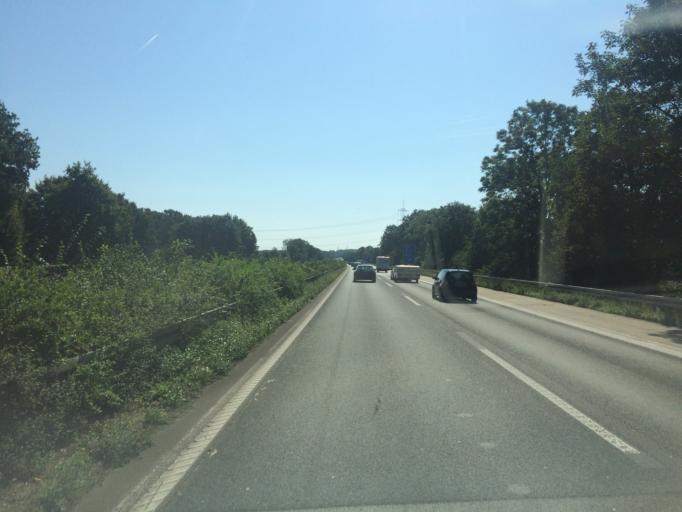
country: DE
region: North Rhine-Westphalia
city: Werne
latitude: 51.6986
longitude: 7.6656
